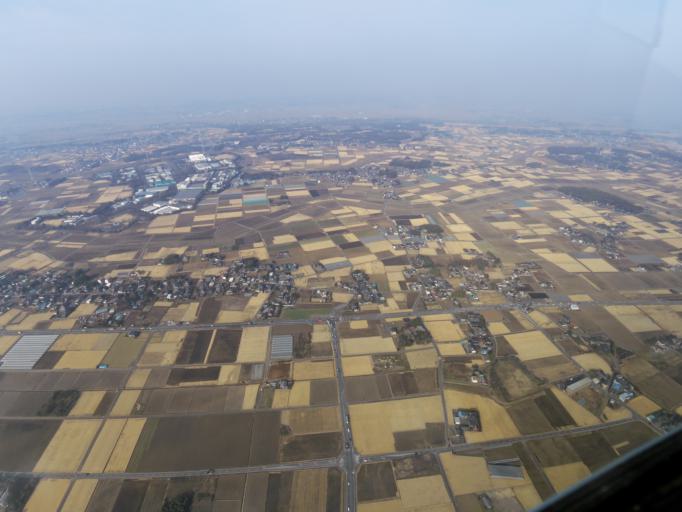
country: JP
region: Ibaraki
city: Ishige
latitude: 36.1197
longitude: 140.0458
